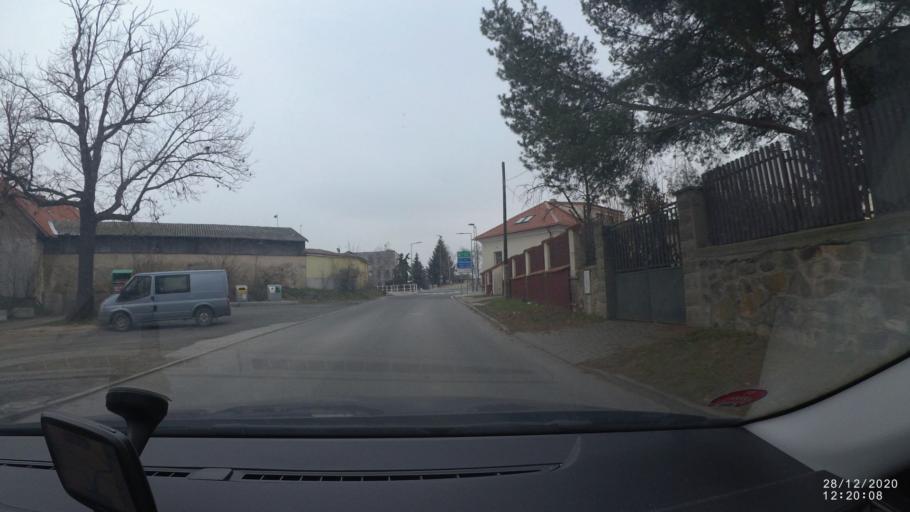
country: CZ
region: Central Bohemia
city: Brandys nad Labem-Stara Boleslav
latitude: 50.1780
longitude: 14.6523
